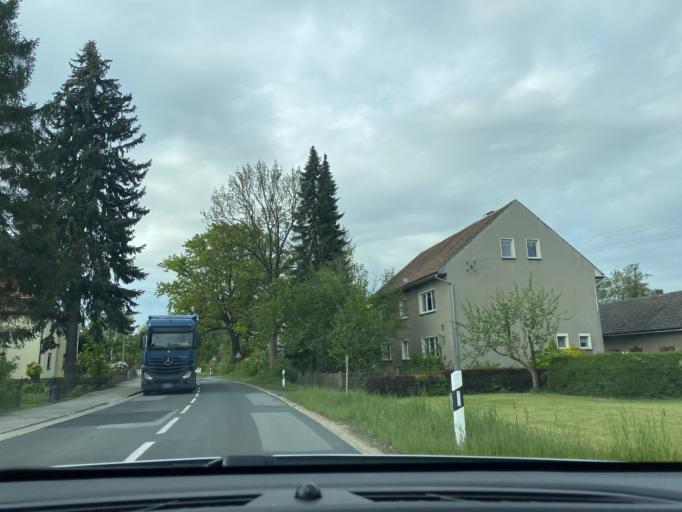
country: DE
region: Saxony
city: Horka
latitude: 51.2999
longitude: 14.8967
